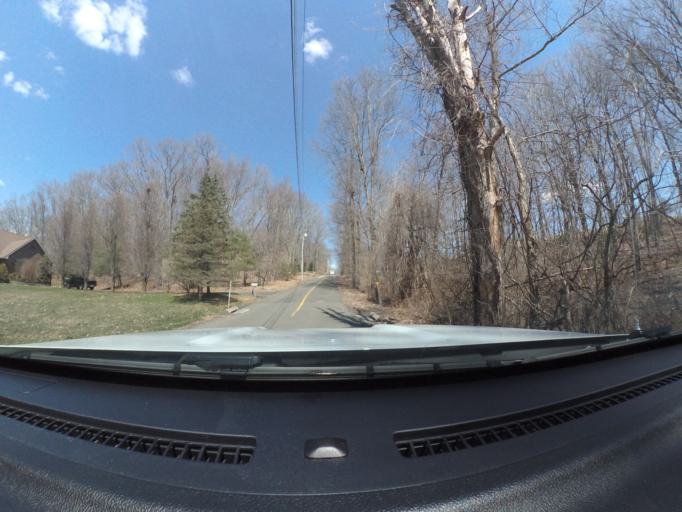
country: US
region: Connecticut
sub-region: Litchfield County
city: Bethlehem Village
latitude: 41.6263
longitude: -73.1650
